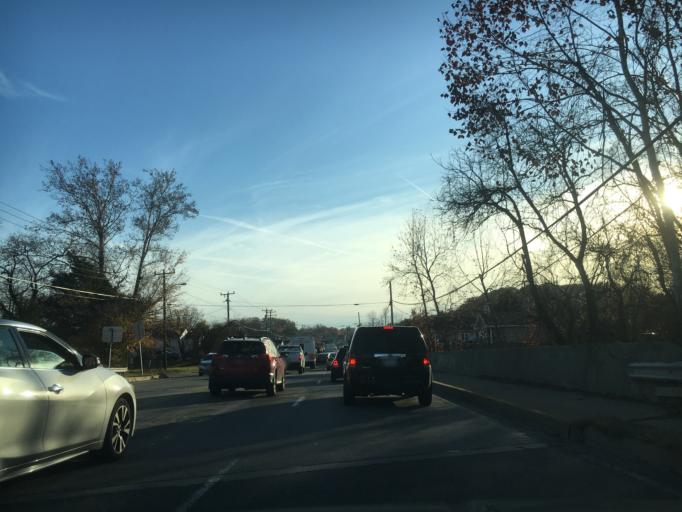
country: US
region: Virginia
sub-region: Prince William County
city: Dumfries
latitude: 38.5661
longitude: -77.3291
